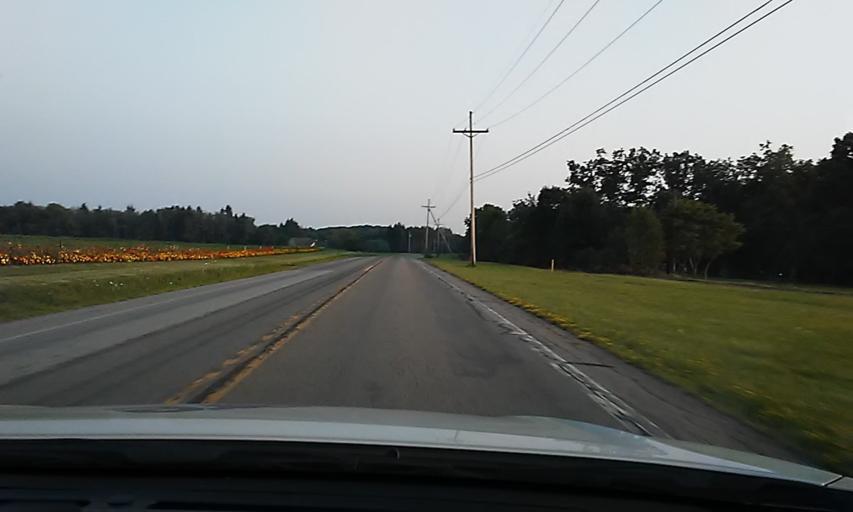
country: US
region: Pennsylvania
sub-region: Clarion County
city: Marianne
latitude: 41.2681
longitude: -79.3908
